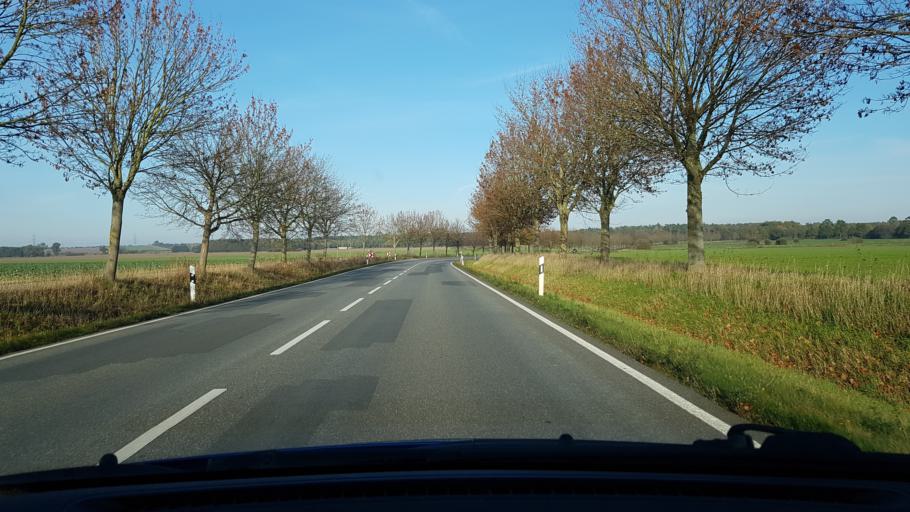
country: DE
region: Mecklenburg-Vorpommern
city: Stralendorf
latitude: 53.5384
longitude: 11.3057
